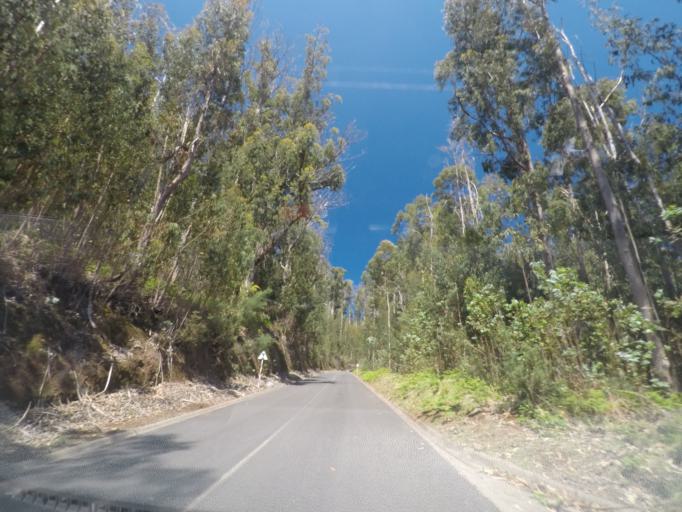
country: PT
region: Madeira
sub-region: Calheta
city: Arco da Calheta
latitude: 32.7377
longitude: -17.1305
